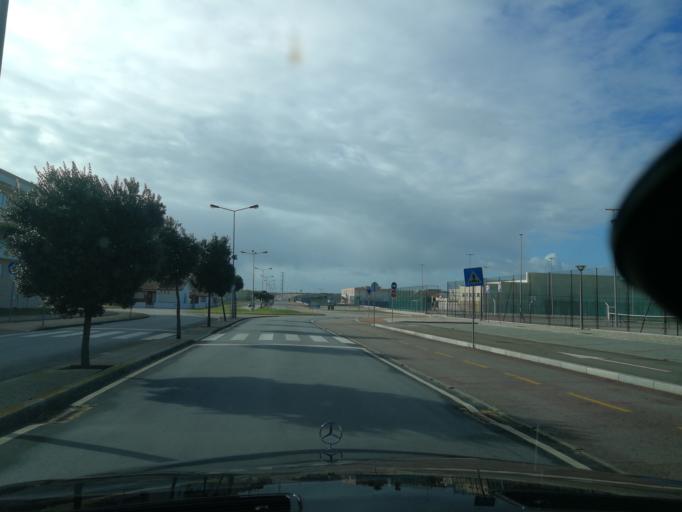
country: PT
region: Aveiro
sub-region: Murtosa
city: Murtosa
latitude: 40.7645
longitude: -8.7039
